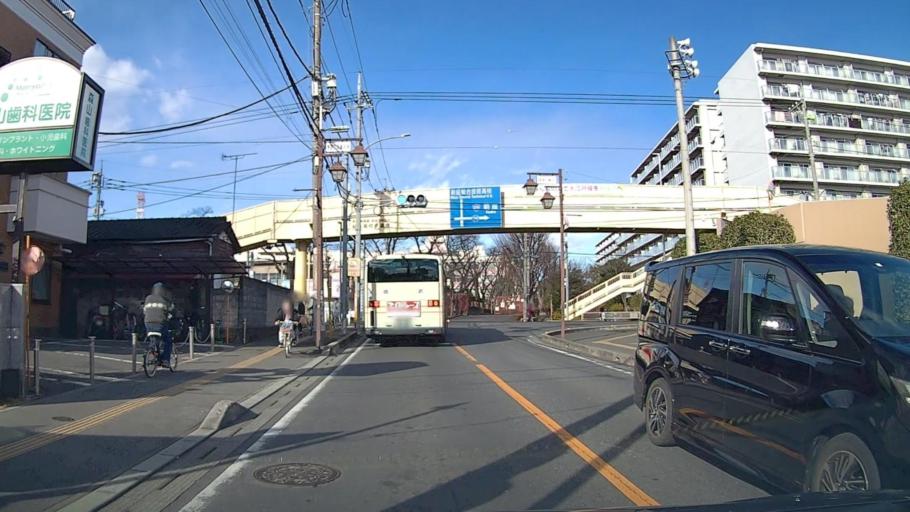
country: JP
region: Saitama
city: Asaka
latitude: 35.7771
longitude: 139.5856
